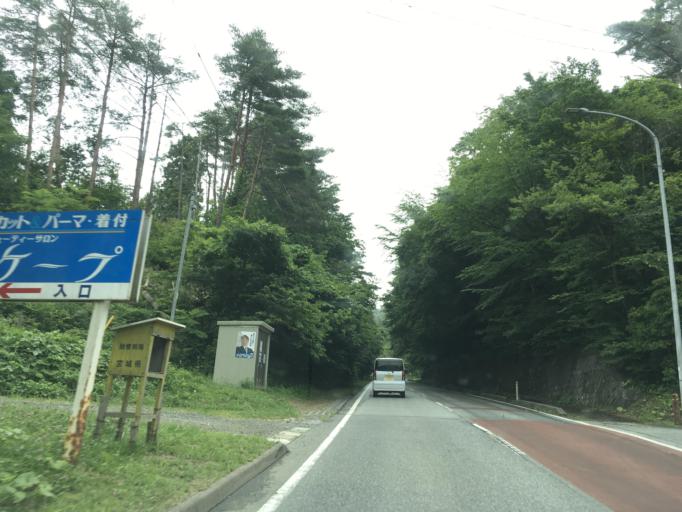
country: JP
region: Iwate
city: Ofunato
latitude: 38.9268
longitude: 141.6379
